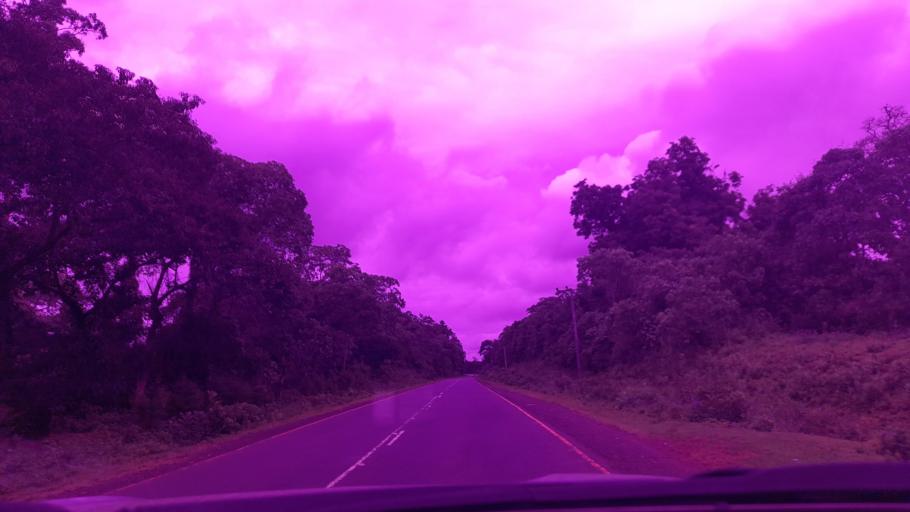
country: ET
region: Southern Nations, Nationalities, and People's Region
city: Bonga
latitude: 7.2825
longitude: 35.9631
